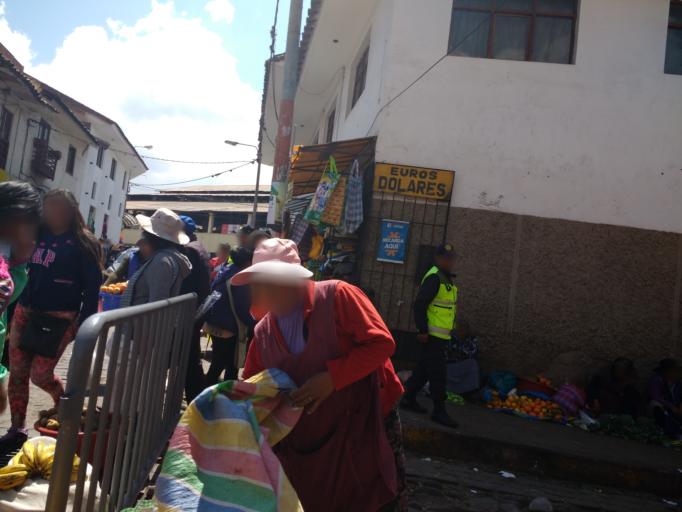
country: PE
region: Cusco
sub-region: Provincia de Cusco
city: Cusco
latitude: -13.5222
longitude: -71.9826
